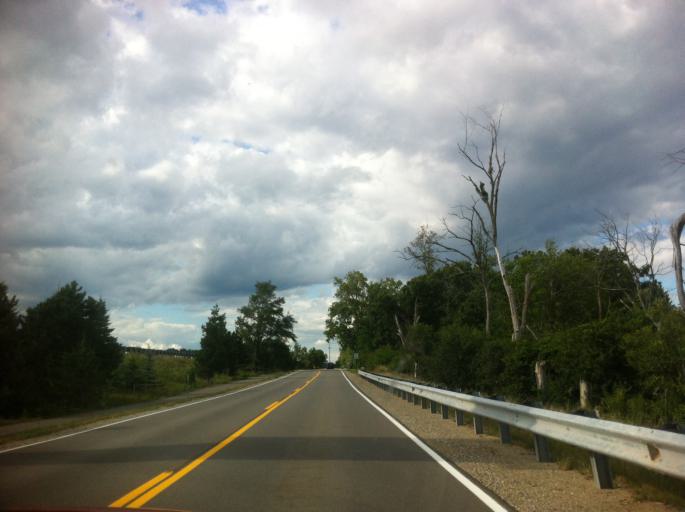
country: US
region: Michigan
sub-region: Livingston County
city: Brighton
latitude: 42.4919
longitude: -83.7569
